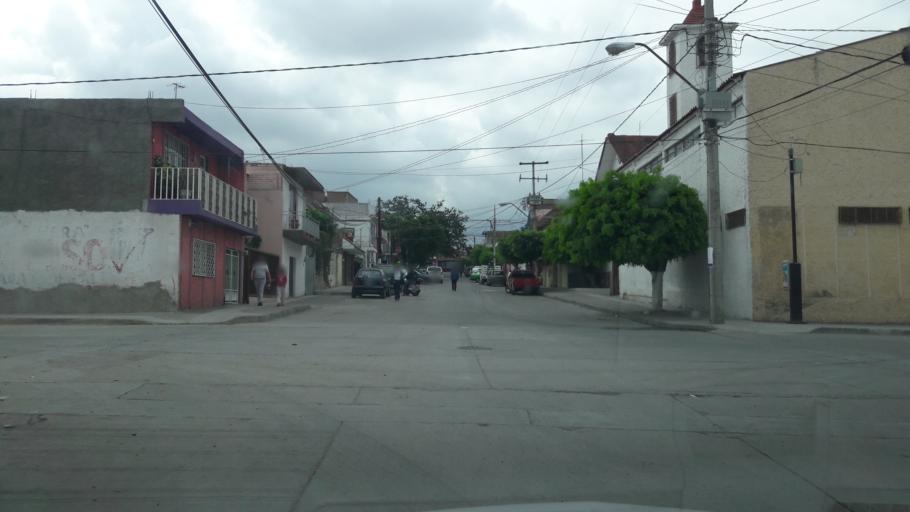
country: MX
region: Guanajuato
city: Leon
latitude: 21.1406
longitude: -101.7010
